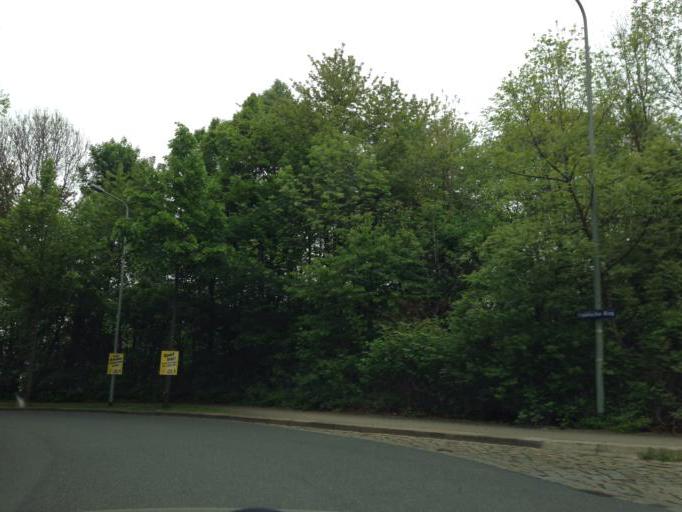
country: DE
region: Saxony
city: Bannewitz
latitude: 51.0222
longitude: 13.7178
